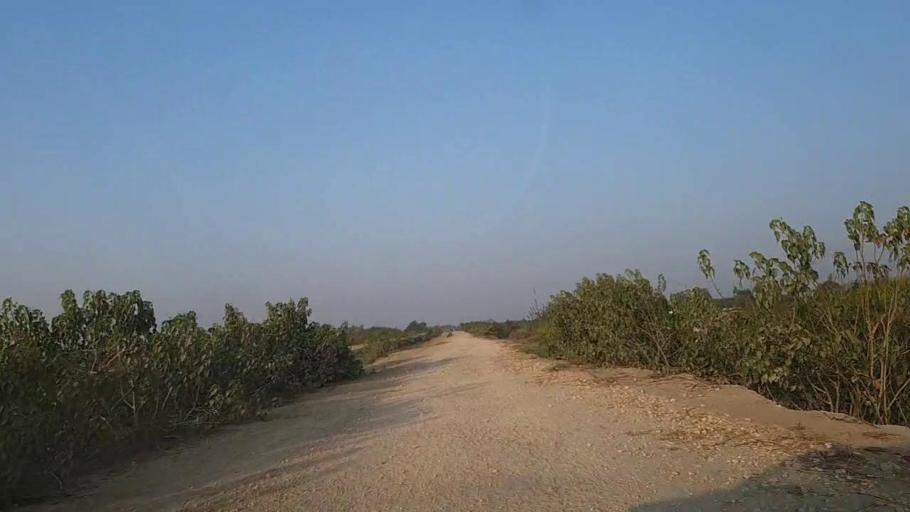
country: PK
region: Sindh
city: Mirpur Sakro
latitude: 24.2830
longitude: 67.6886
